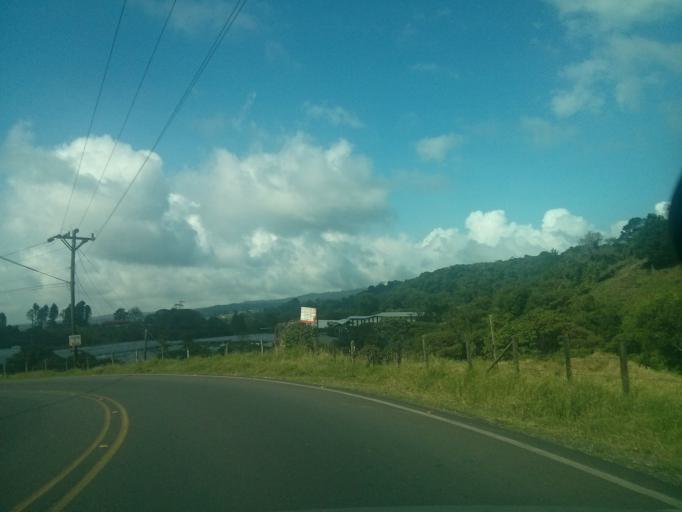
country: CR
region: Heredia
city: Santo Domingo
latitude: 10.1623
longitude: -84.1551
